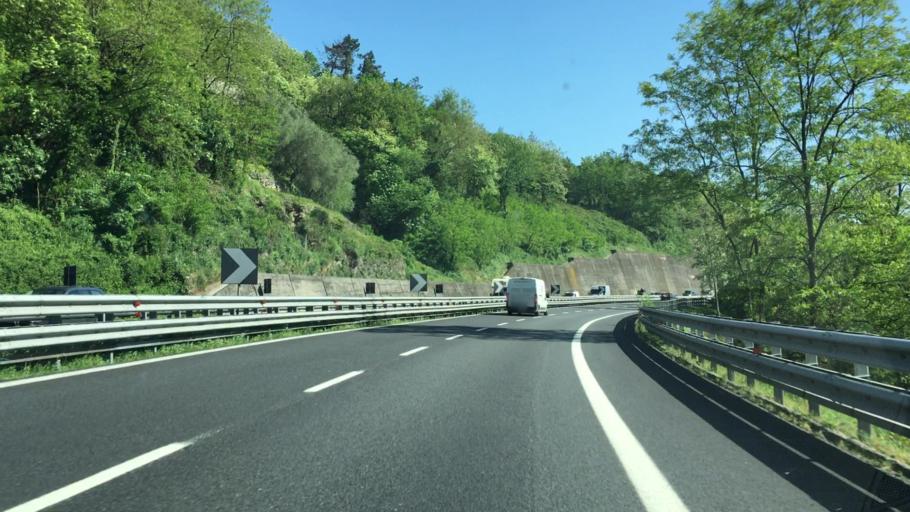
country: IT
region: Liguria
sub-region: Provincia di Genova
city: Cogorno
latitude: 44.3008
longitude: 9.3838
